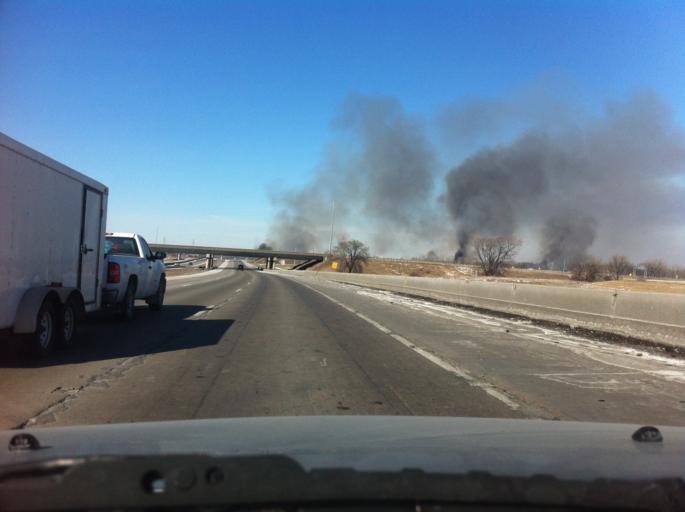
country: US
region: Wisconsin
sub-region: Columbia County
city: Portage
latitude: 43.4566
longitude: -89.4979
